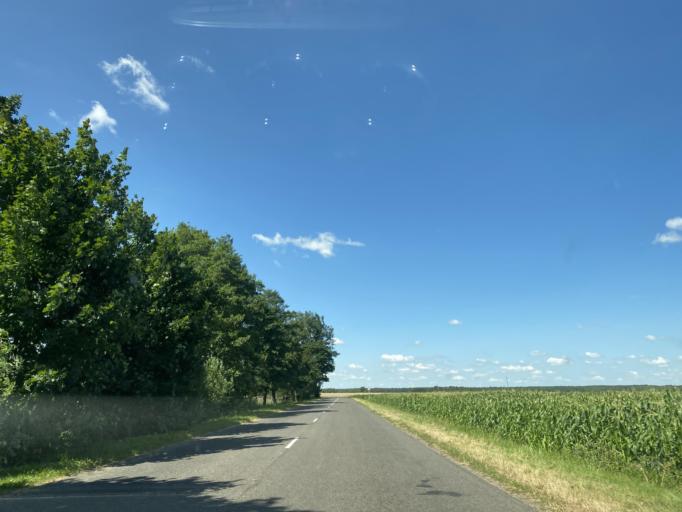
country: BY
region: Brest
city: Ivanava
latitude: 52.2074
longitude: 25.6244
